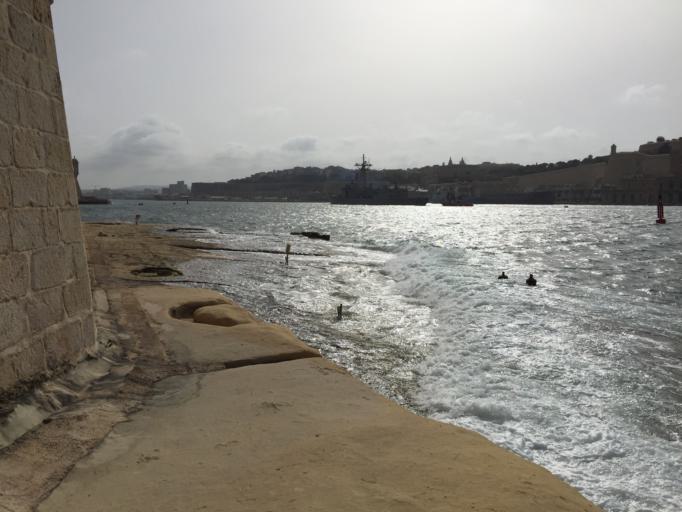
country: MT
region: Il-Birgu
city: Vittoriosa
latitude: 35.8929
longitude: 14.5175
